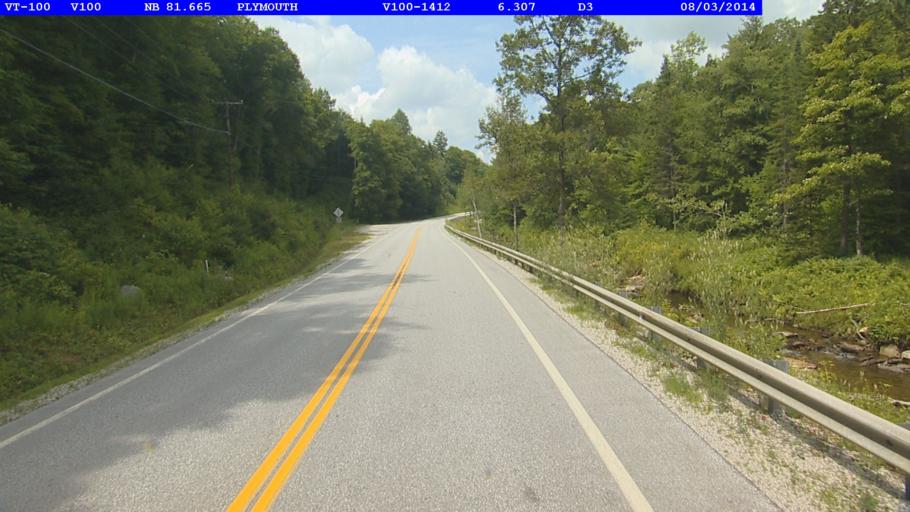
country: US
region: Vermont
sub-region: Rutland County
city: Rutland
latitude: 43.5420
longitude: -72.7487
